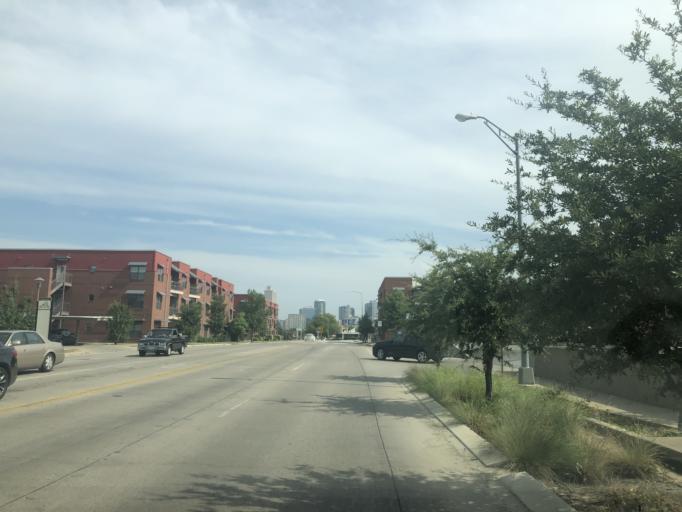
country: US
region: Texas
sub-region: Tarrant County
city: Fort Worth
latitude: 32.7333
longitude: -97.3315
